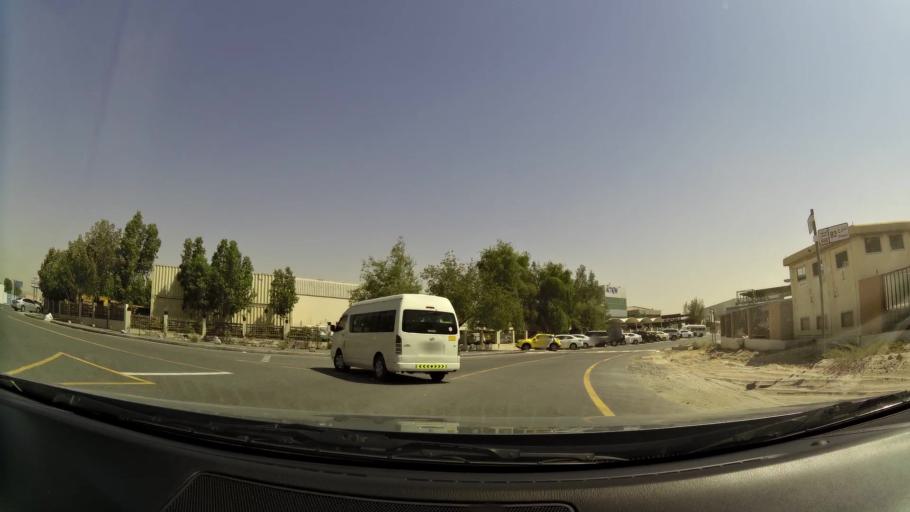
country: AE
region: Dubai
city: Dubai
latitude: 24.9703
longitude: 55.1794
